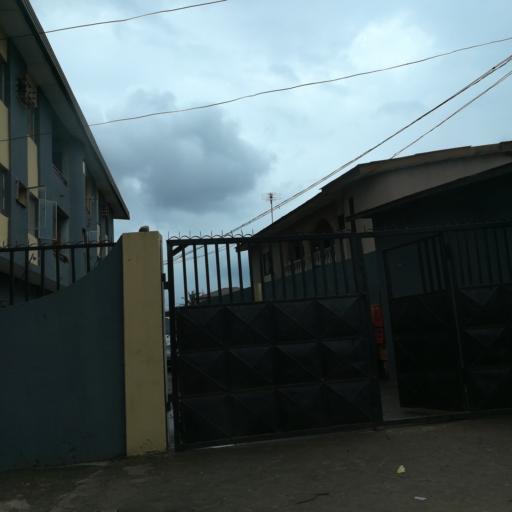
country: NG
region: Lagos
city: Agege
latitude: 6.6069
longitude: 3.3016
